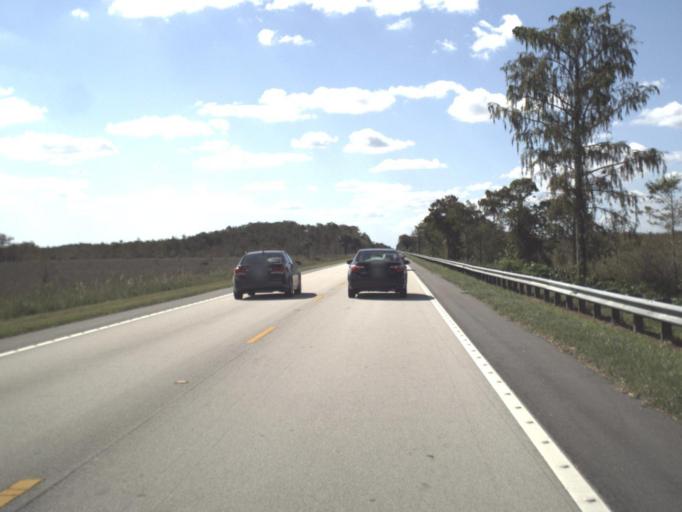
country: US
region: Florida
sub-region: Collier County
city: Immokalee
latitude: 25.8621
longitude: -81.0841
